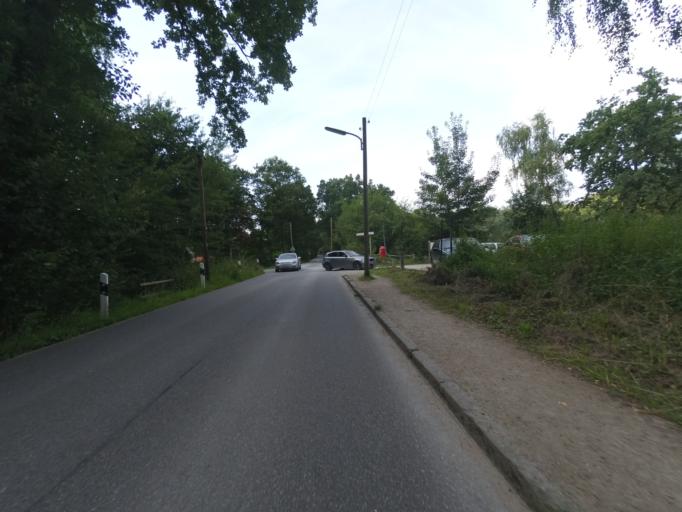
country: DE
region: Schleswig-Holstein
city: Oststeinbek
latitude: 53.5093
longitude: 10.1614
